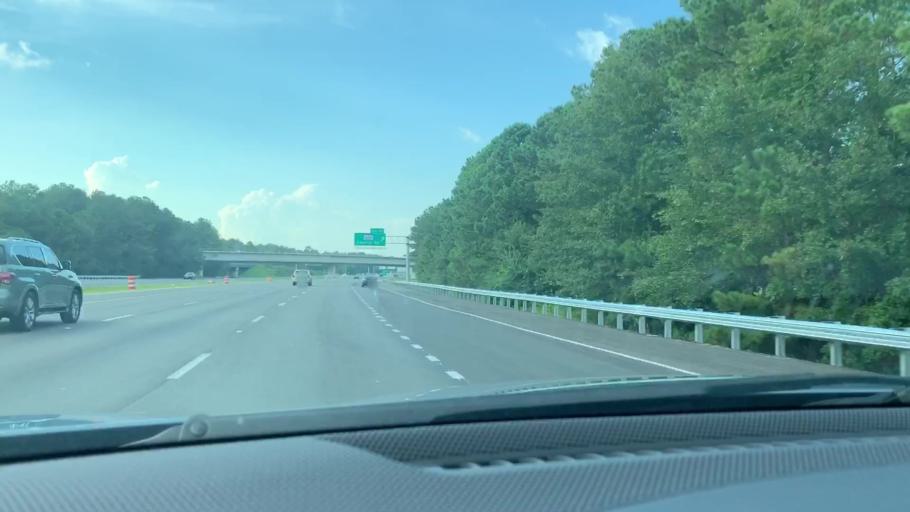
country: US
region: South Carolina
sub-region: Richland County
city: Dentsville
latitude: 34.0911
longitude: -80.9521
